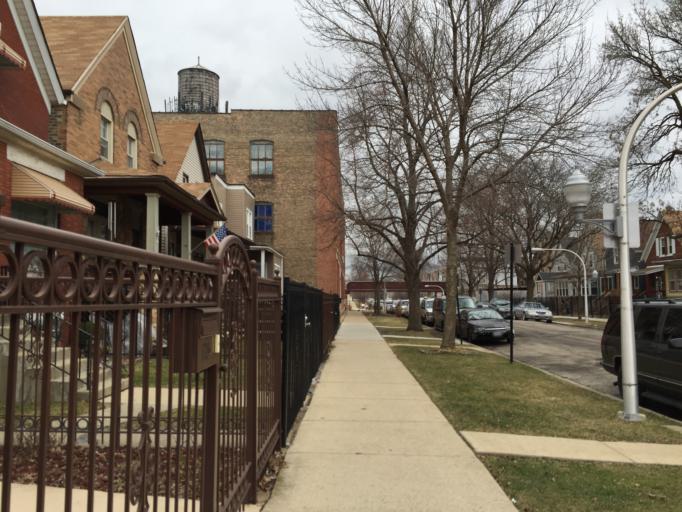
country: US
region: Illinois
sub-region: Cook County
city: Oak Park
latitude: 41.9126
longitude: -87.7192
